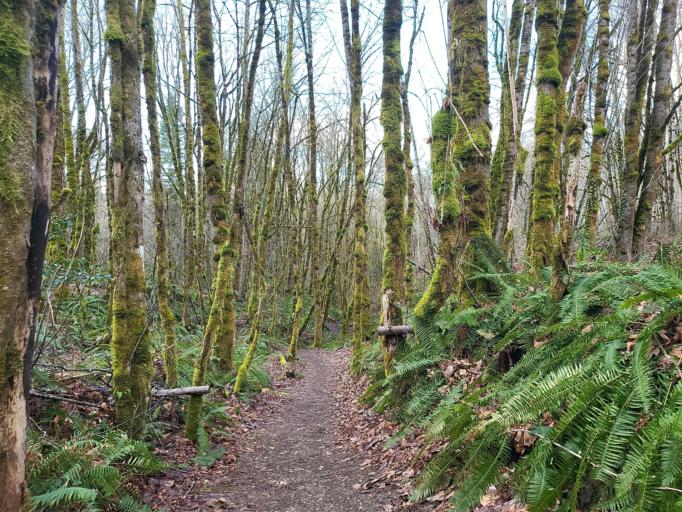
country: US
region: Washington
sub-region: King County
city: Newcastle
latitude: 47.5327
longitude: -122.1251
